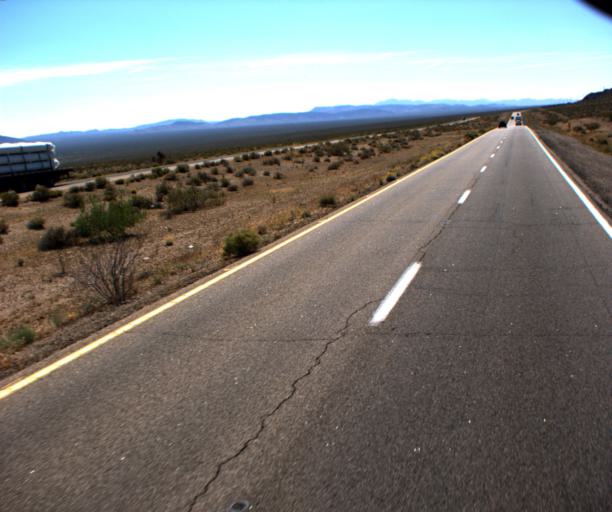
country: US
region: Arizona
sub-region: Mohave County
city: Dolan Springs
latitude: 35.7982
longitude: -114.5333
